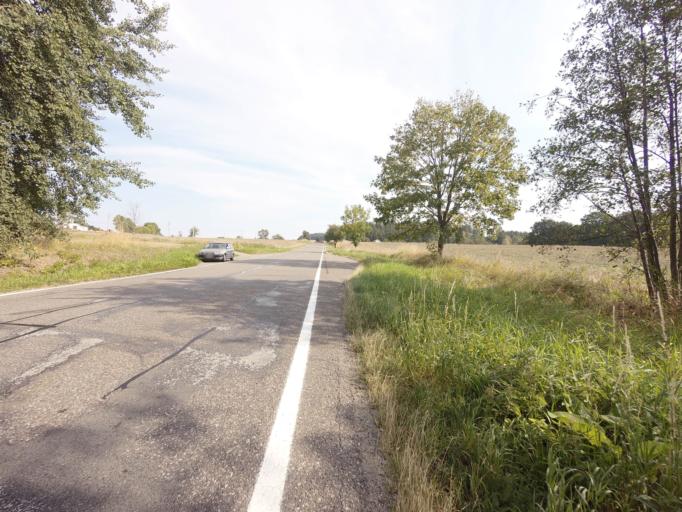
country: CZ
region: Jihocesky
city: Milevsko
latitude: 49.4991
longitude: 14.3624
